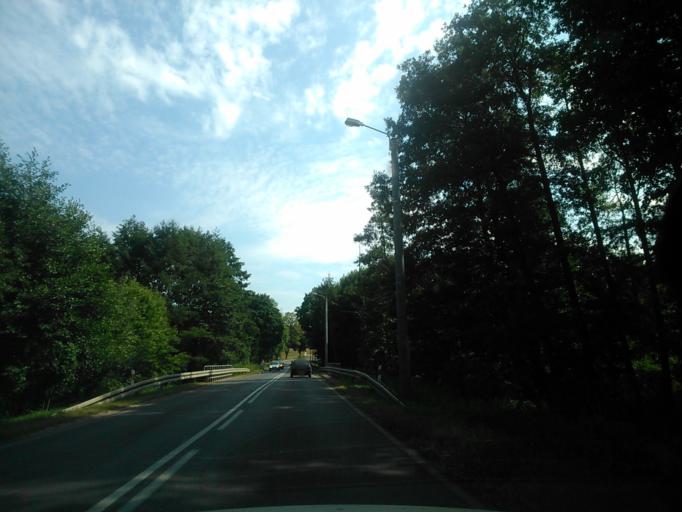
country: PL
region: Warmian-Masurian Voivodeship
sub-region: Powiat dzialdowski
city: Ilowo -Osada
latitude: 53.1480
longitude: 20.3343
